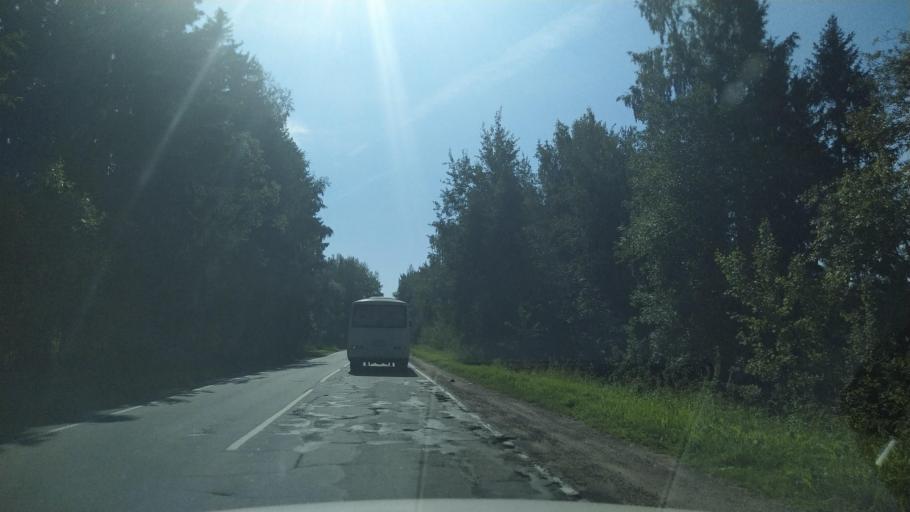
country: RU
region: Leningrad
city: Siverskiy
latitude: 59.3322
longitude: 30.0597
